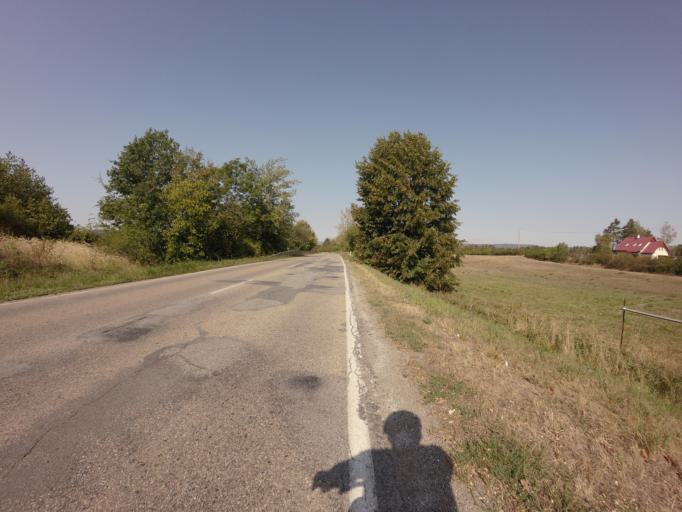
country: CZ
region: Central Bohemia
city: Tynec nad Sazavou
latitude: 49.8259
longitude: 14.6191
